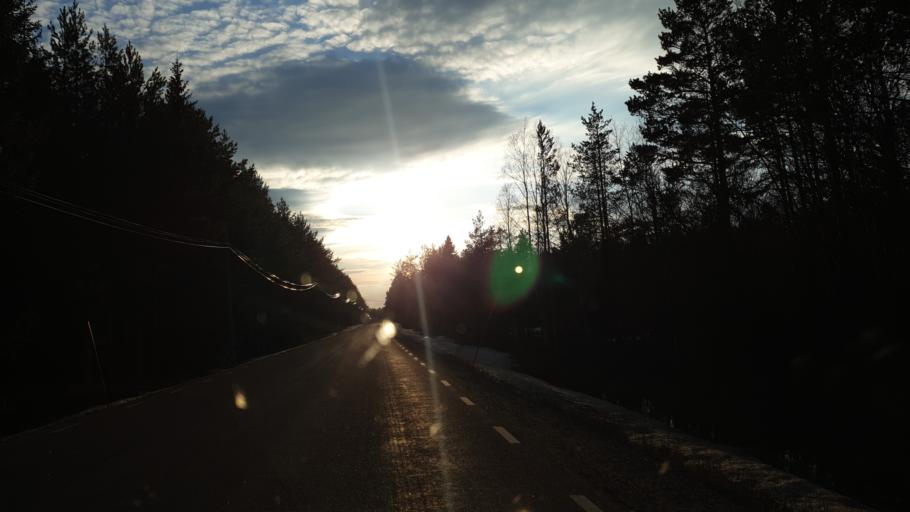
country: SE
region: Vaesternorrland
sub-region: Sundsvalls Kommun
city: Njurundabommen
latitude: 62.2449
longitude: 17.5066
